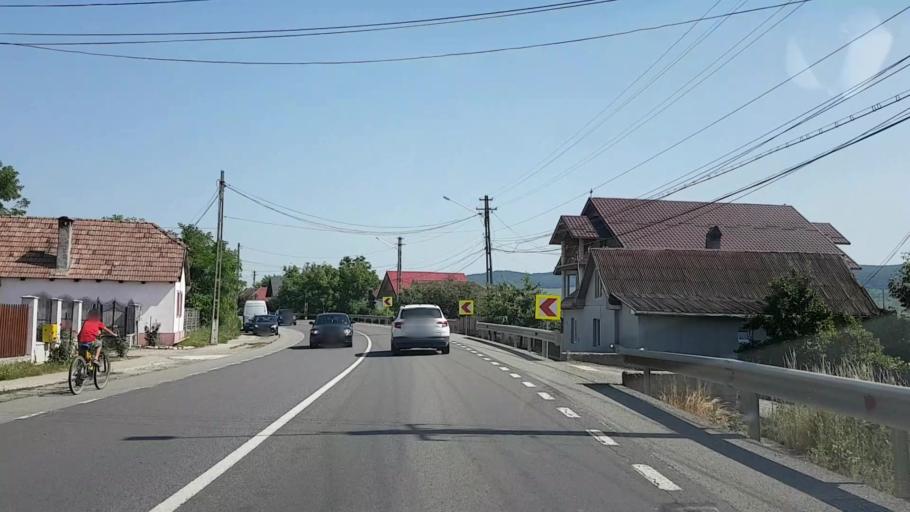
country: RO
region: Bistrita-Nasaud
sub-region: Comuna Sieu-Magherus
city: Sieu-Magherus
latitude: 47.0950
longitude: 24.3686
